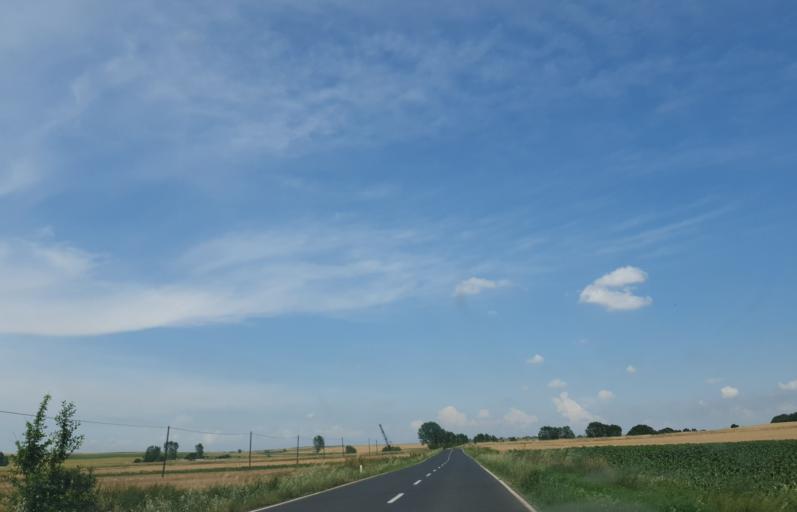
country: TR
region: Tekirdag
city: Muratli
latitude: 41.2237
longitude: 27.5539
